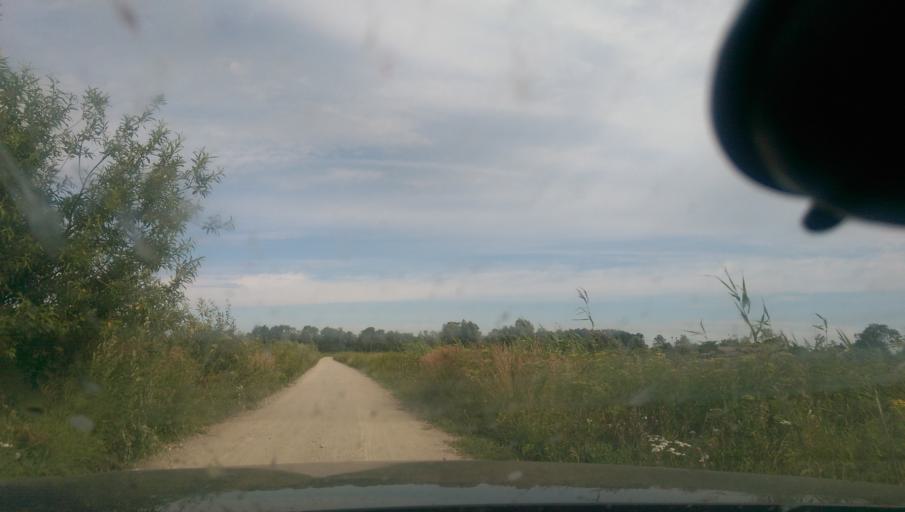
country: LT
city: Rusne
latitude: 55.2940
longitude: 21.3490
